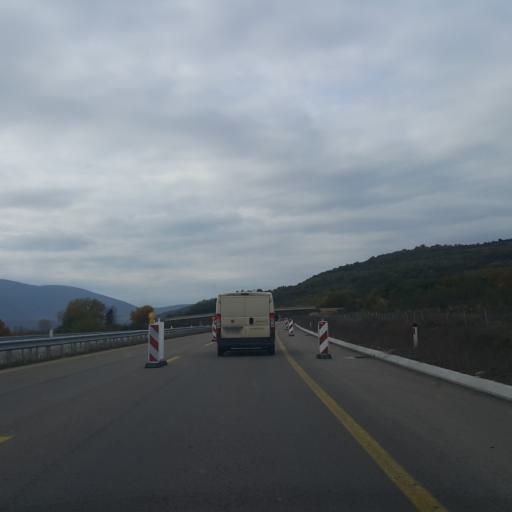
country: RS
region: Central Serbia
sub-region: Pirotski Okrug
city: Bela Palanka
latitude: 43.2352
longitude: 22.3671
